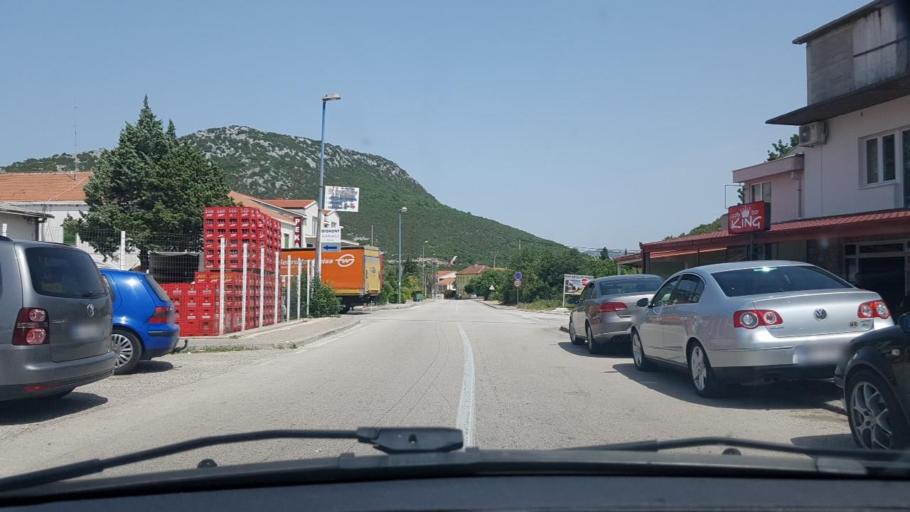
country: BA
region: Federation of Bosnia and Herzegovina
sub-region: Hercegovacko-Bosanski Kanton
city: Neum
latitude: 42.9249
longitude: 17.6223
